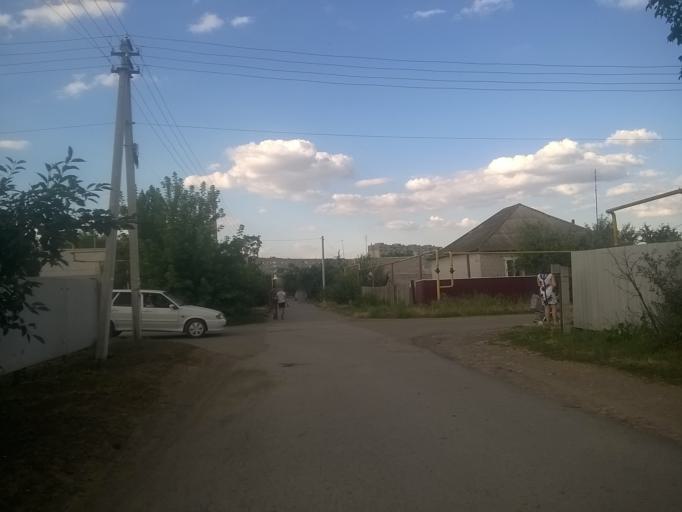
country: RU
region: Rostov
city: Donetsk
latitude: 48.3425
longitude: 39.9625
